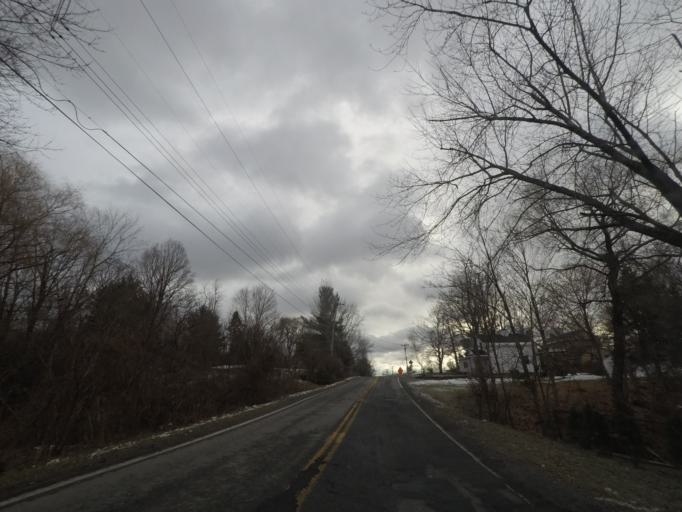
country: US
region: New York
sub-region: Rensselaer County
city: East Greenbush
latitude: 42.5967
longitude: -73.7196
